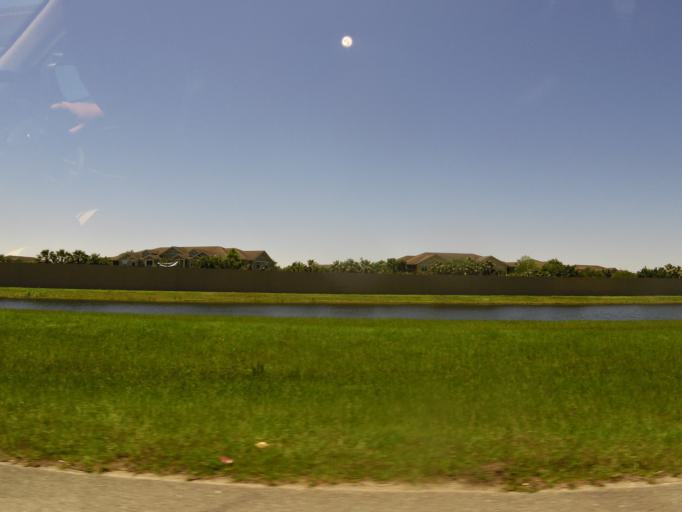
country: US
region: Florida
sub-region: Saint Johns County
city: Fruit Cove
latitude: 30.1149
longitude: -81.5156
